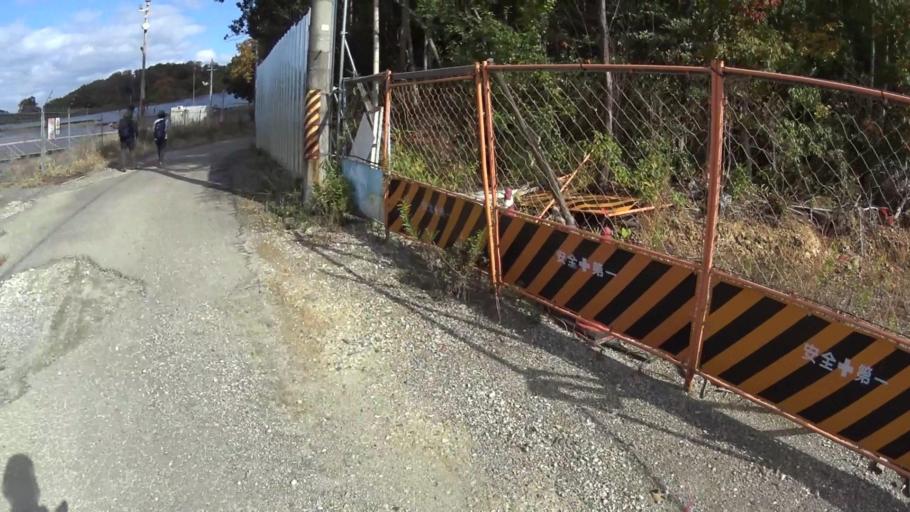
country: JP
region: Kyoto
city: Uji
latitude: 34.9479
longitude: 135.7909
